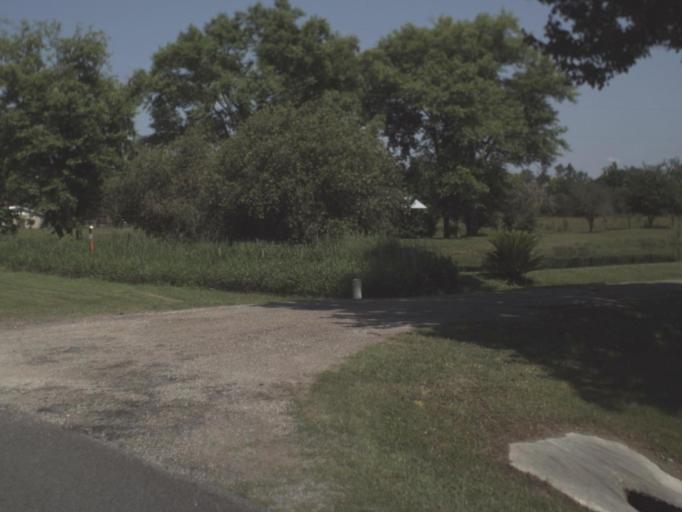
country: US
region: Florida
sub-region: Clay County
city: Green Cove Springs
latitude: 29.9837
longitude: -81.7331
